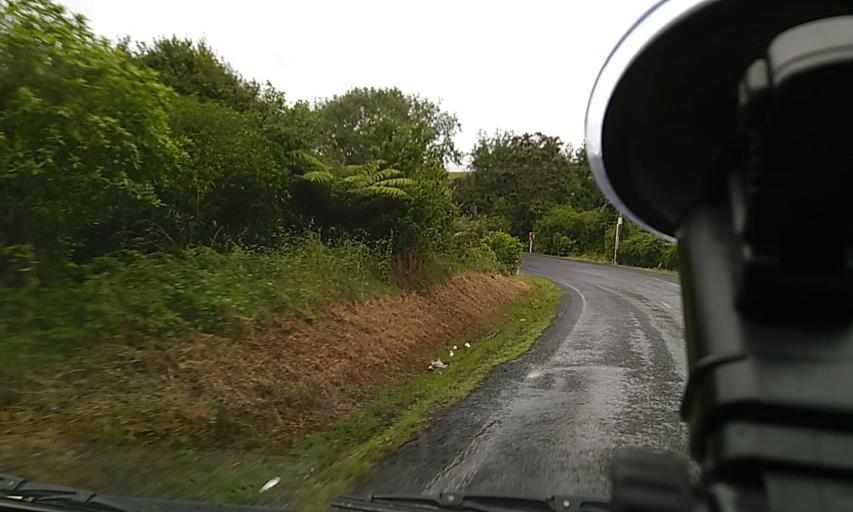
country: NZ
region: Auckland
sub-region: Auckland
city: Pukekohe East
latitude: -37.3018
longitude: 174.9384
